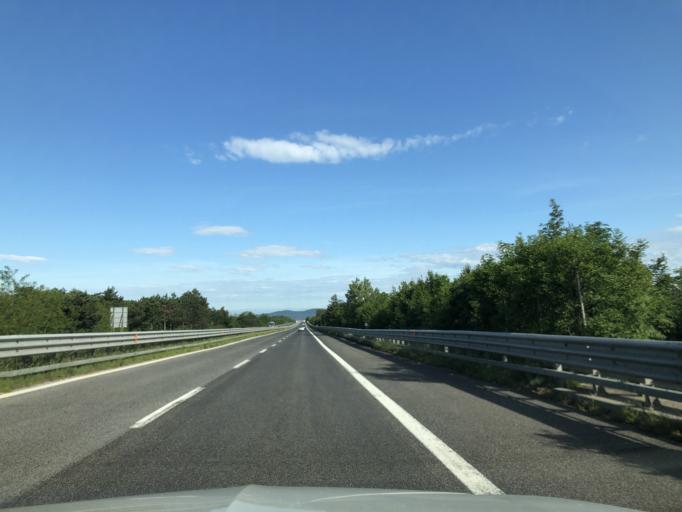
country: IT
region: Friuli Venezia Giulia
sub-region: Provincia di Trieste
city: Santa Croce
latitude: 45.7271
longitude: 13.7161
